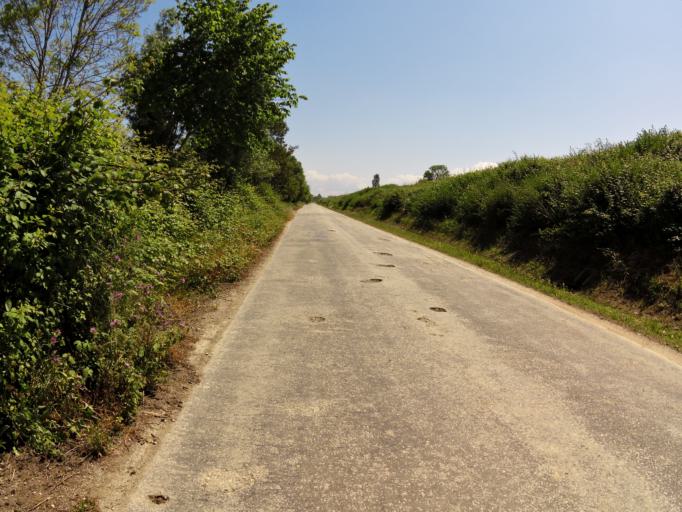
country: PT
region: Coimbra
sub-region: Montemor-O-Velho
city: Montemor-o-Velho
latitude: 40.1488
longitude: -8.7291
